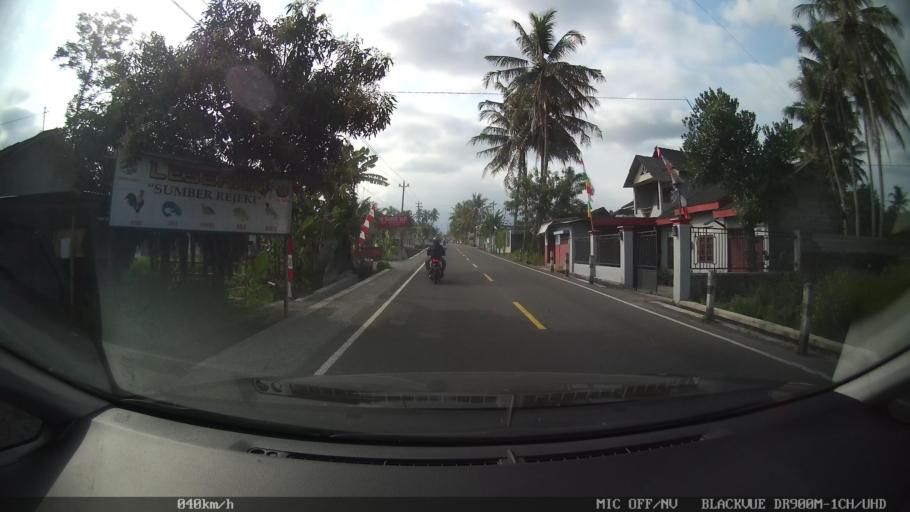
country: ID
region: Central Java
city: Candi Prambanan
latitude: -7.6929
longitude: 110.4629
